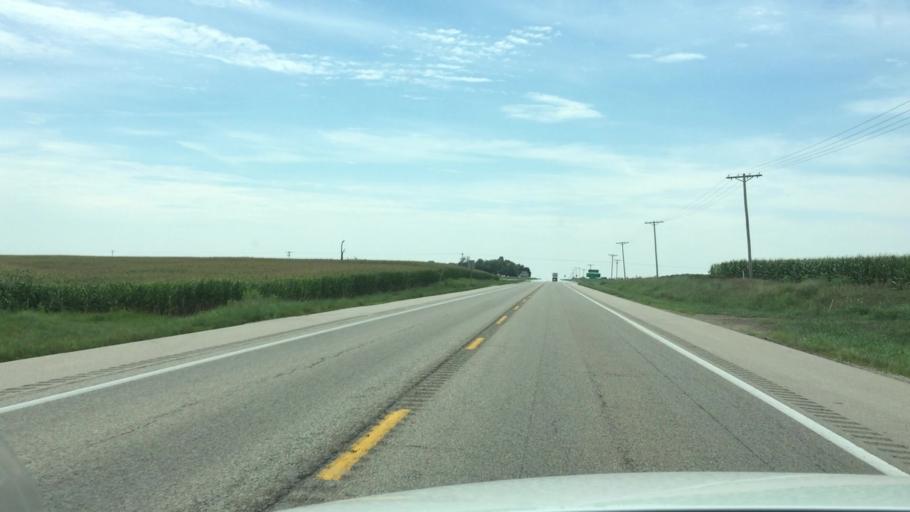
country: US
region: Kansas
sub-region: Nemaha County
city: Sabetha
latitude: 39.7575
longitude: -95.7297
